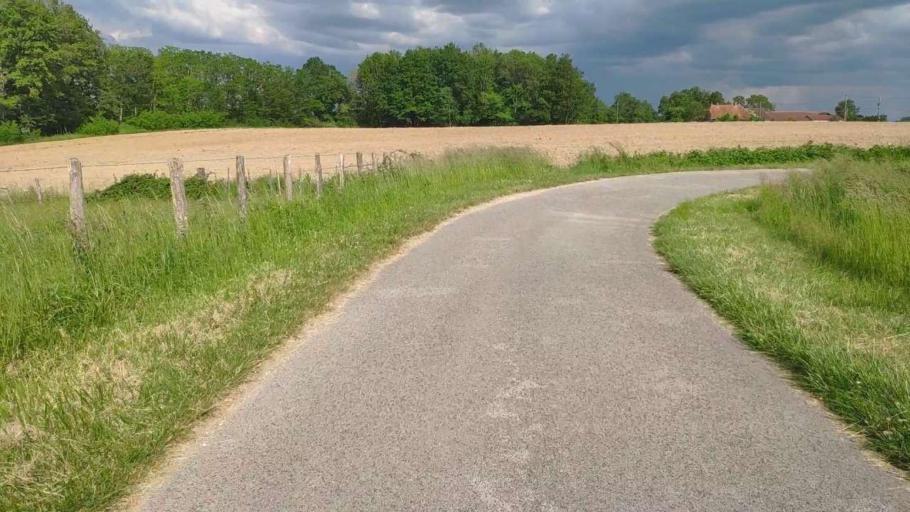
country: FR
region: Bourgogne
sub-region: Departement de Saone-et-Loire
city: Pierre-de-Bresse
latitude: 46.8204
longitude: 5.3396
